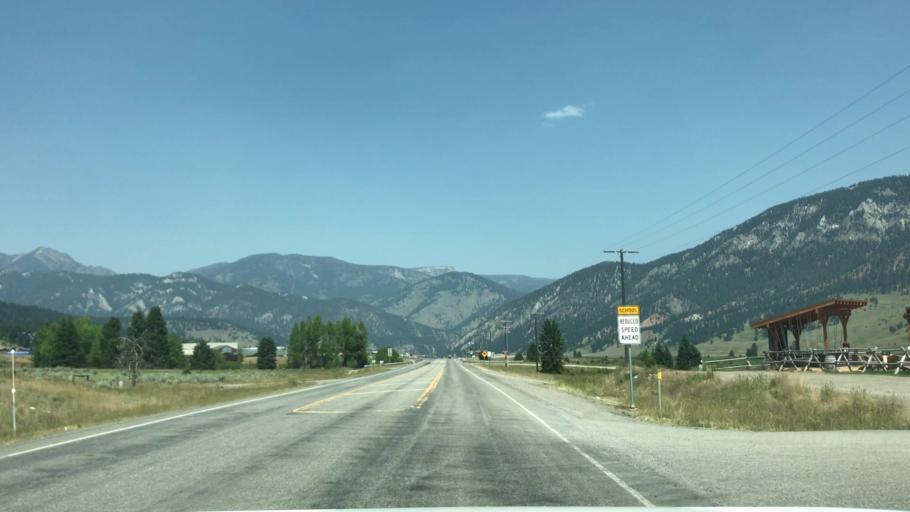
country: US
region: Montana
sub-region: Gallatin County
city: Big Sky
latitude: 45.2239
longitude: -111.2508
